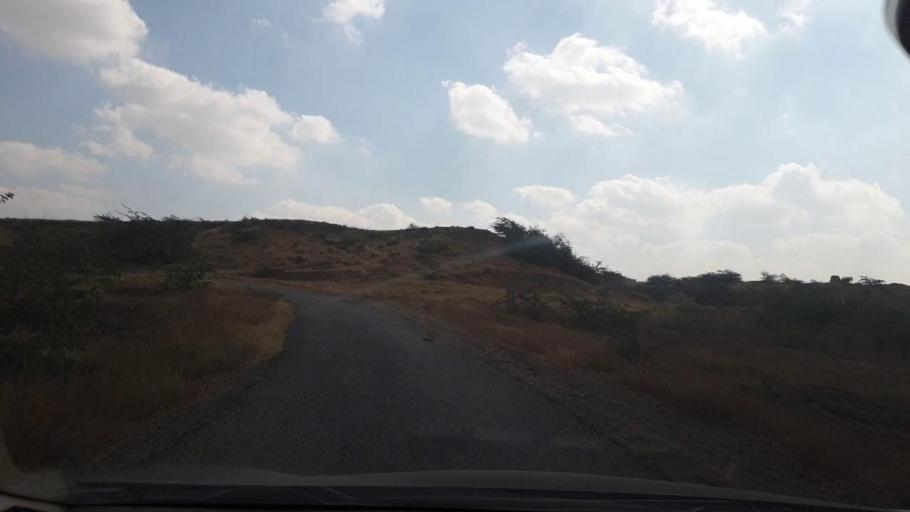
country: PK
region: Sindh
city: Malir Cantonment
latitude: 25.0247
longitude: 67.3503
